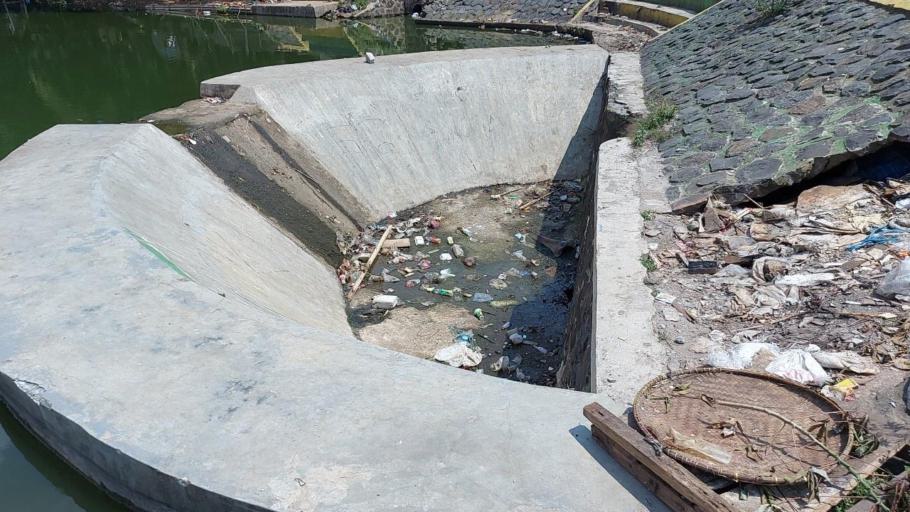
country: ID
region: West Java
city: Cibinong
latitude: -6.4705
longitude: 106.8481
